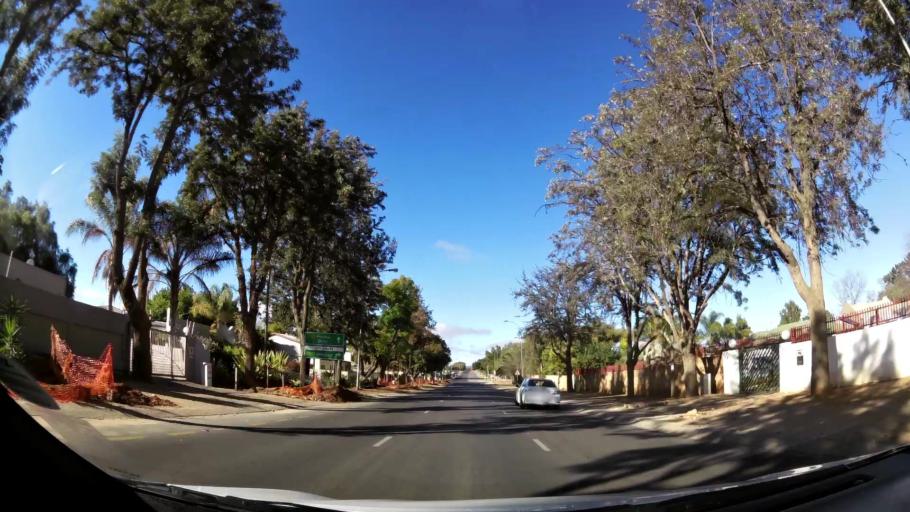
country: ZA
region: Limpopo
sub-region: Capricorn District Municipality
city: Polokwane
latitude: -23.9176
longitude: 29.4619
